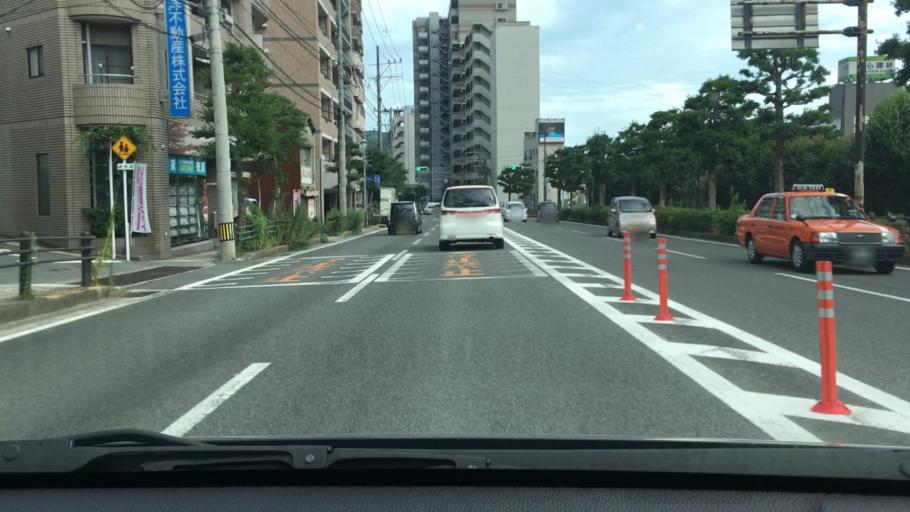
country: JP
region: Nagasaki
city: Obita
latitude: 32.7957
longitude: 129.8555
